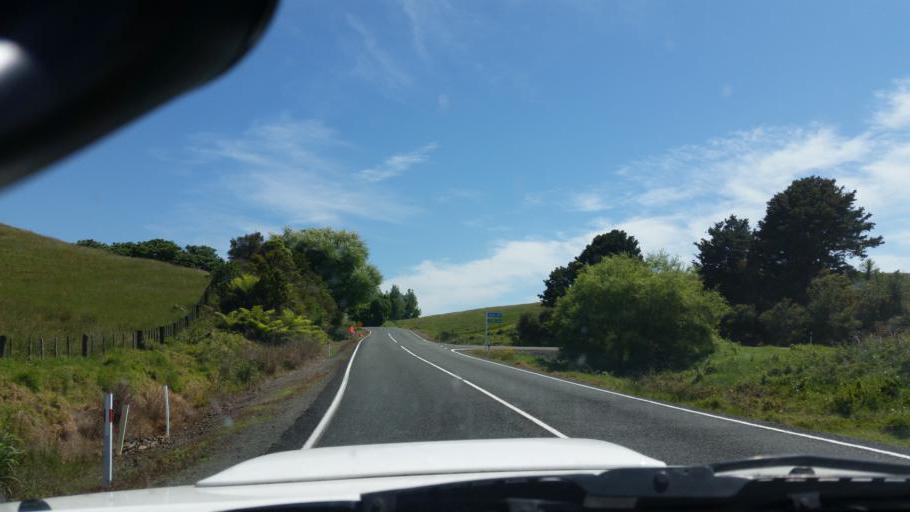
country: NZ
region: Auckland
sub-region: Auckland
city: Wellsford
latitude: -36.1849
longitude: 174.4117
